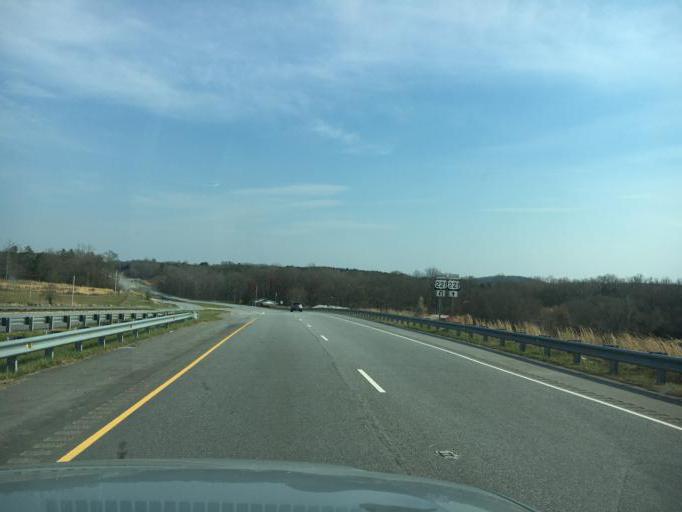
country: US
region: North Carolina
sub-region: Rutherford County
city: Forest City
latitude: 35.2490
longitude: -81.8720
